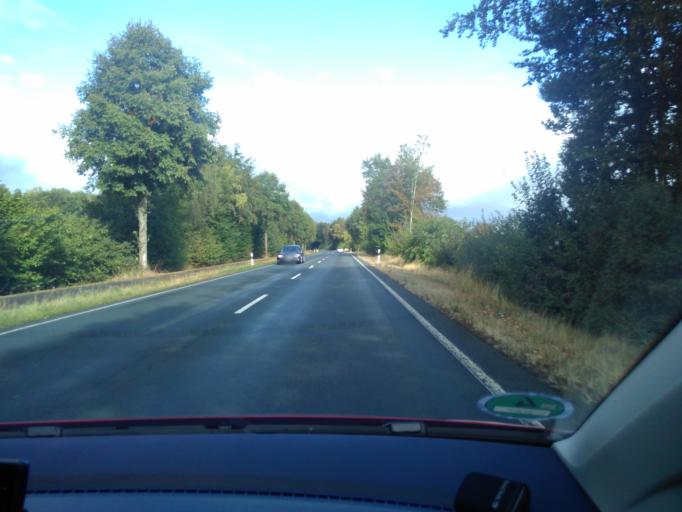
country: DE
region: North Rhine-Westphalia
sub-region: Regierungsbezirk Munster
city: Ostbevern
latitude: 52.0106
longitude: 7.9215
